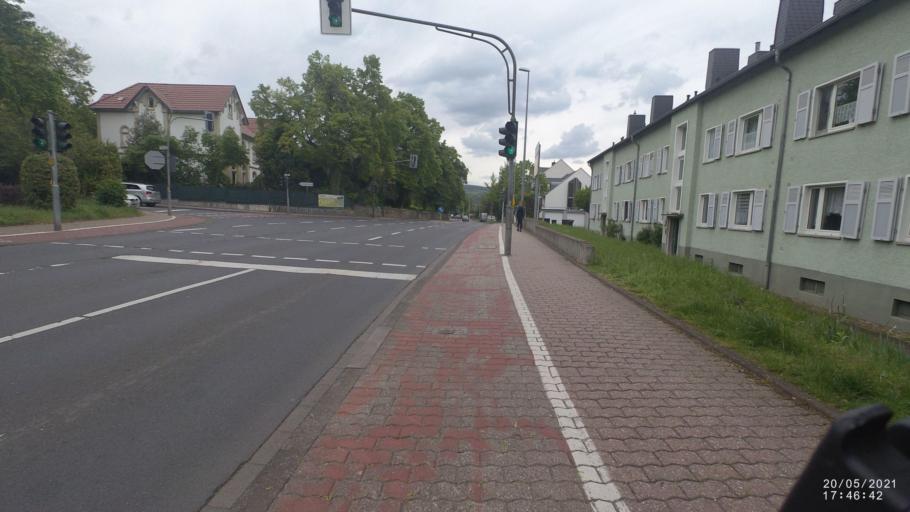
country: DE
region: Rheinland-Pfalz
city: Andernach
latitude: 50.4278
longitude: 7.4040
